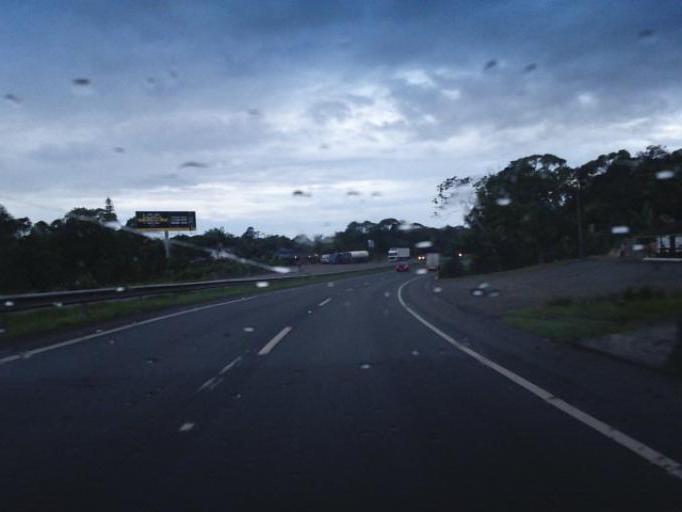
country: BR
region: Santa Catarina
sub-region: Joinville
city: Joinville
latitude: -26.0139
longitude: -48.8621
